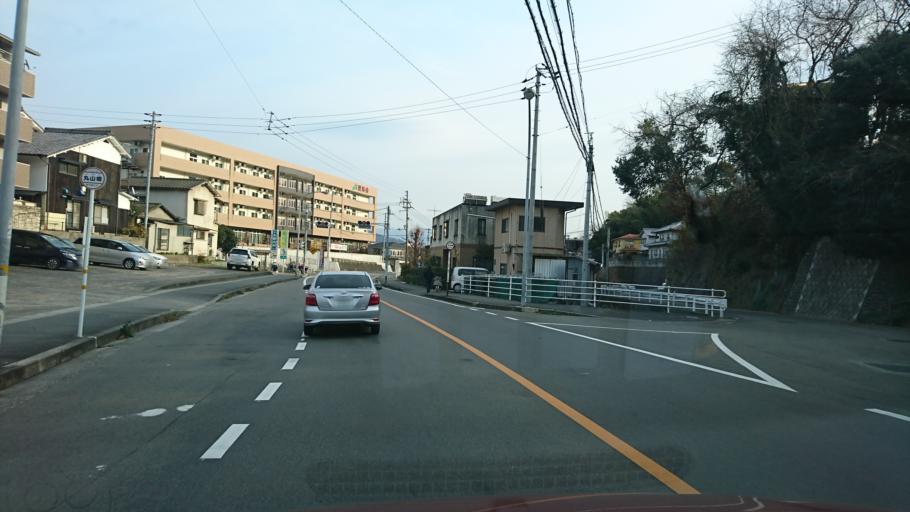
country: JP
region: Ehime
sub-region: Shikoku-chuo Shi
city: Matsuyama
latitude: 33.8615
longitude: 132.7757
